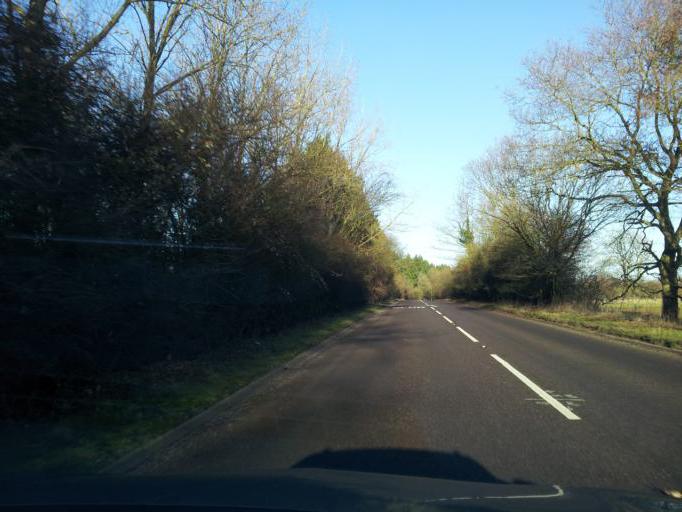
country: GB
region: England
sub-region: Suffolk
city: Lavenham
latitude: 52.1326
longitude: 0.7530
